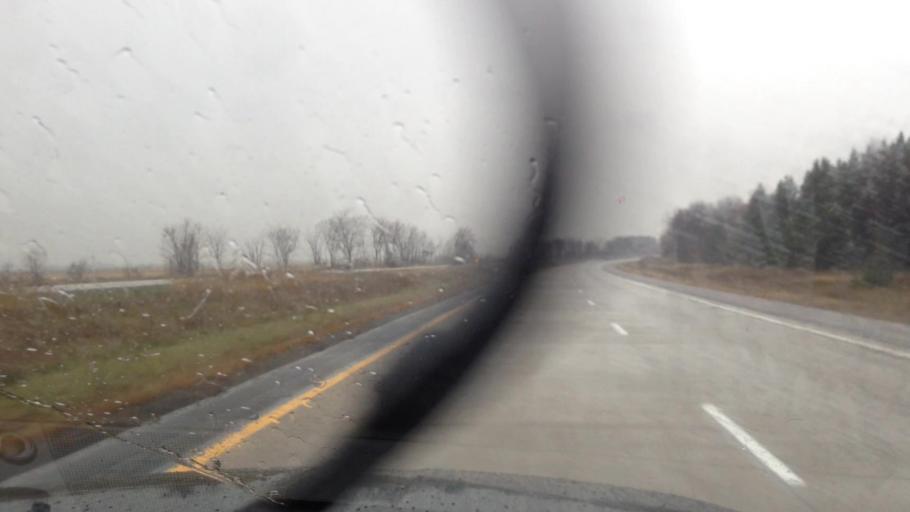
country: CA
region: Ontario
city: Hawkesbury
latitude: 45.4124
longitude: -74.7698
